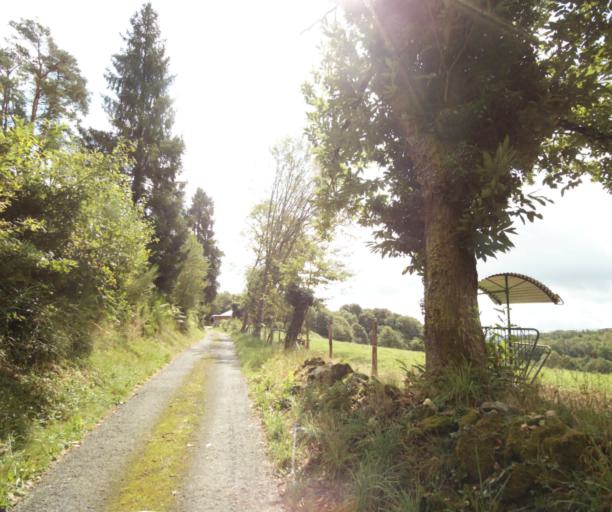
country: FR
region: Limousin
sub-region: Departement de la Correze
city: Sainte-Fortunade
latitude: 45.1720
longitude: 1.7861
